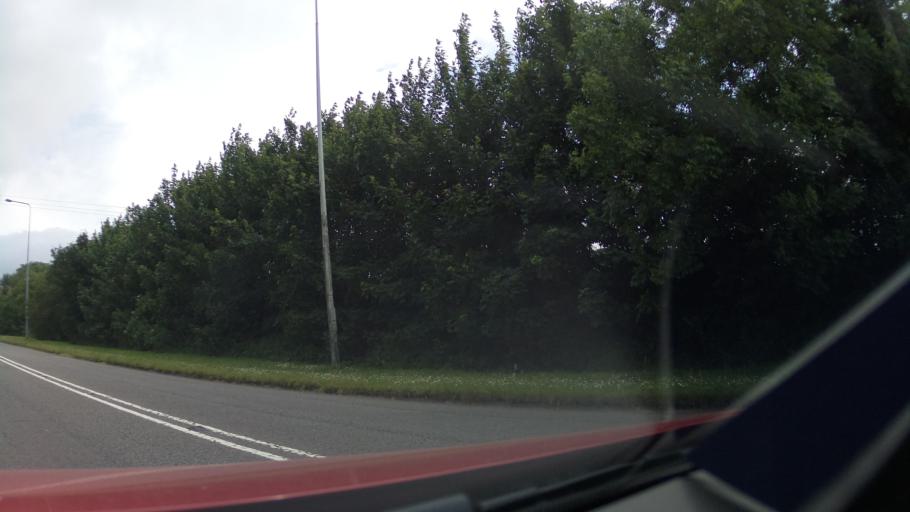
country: GB
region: Wales
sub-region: Vale of Glamorgan
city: Barry
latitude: 51.4593
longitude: -3.3184
